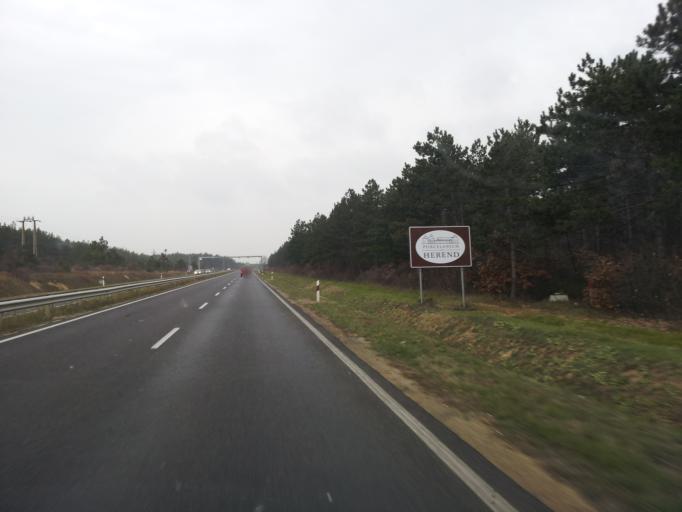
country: HU
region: Veszprem
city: Nemesvamos
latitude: 47.1135
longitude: 17.8516
